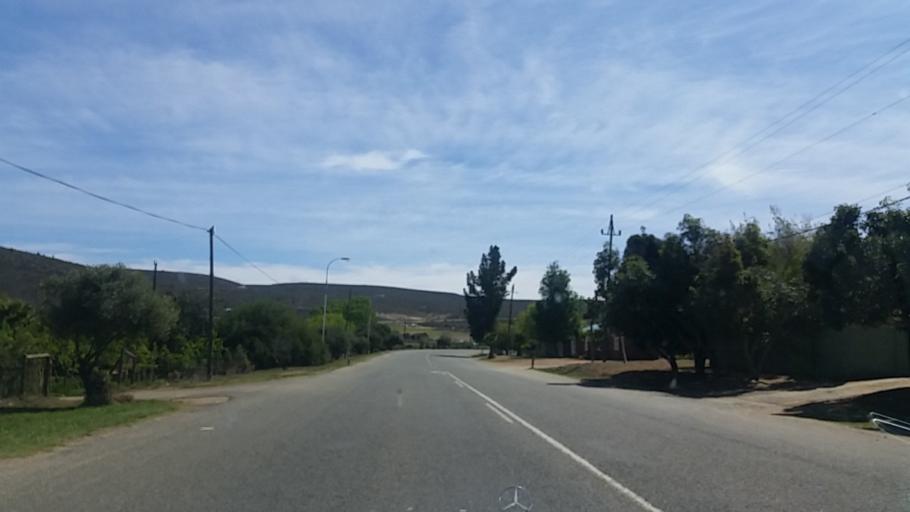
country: ZA
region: Western Cape
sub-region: Eden District Municipality
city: Knysna
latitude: -33.6510
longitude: 23.1347
